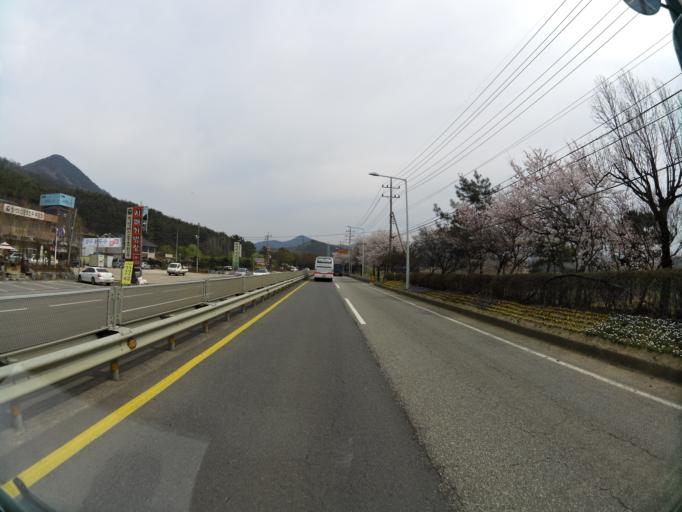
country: KR
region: Gyeongsangnam-do
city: Changnyeong
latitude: 35.4485
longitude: 128.5321
